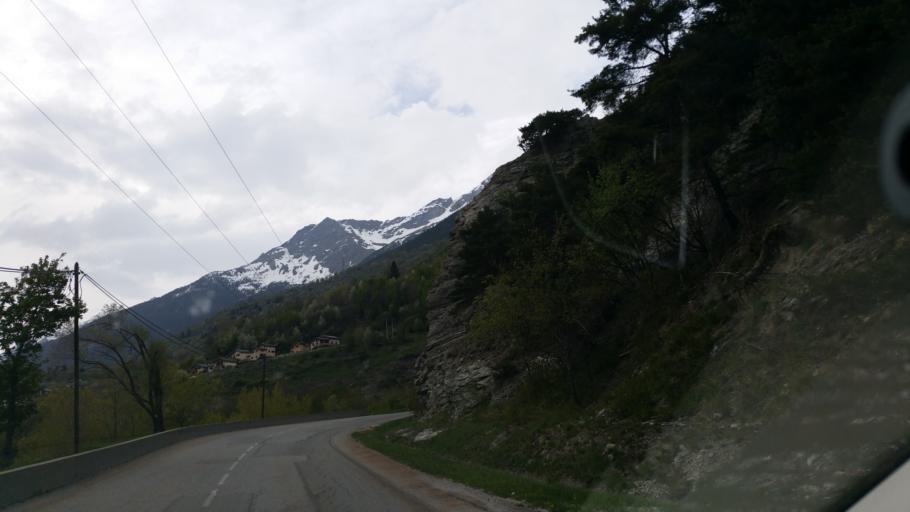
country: FR
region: Rhone-Alpes
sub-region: Departement de la Savoie
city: Modane
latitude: 45.1974
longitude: 6.6278
